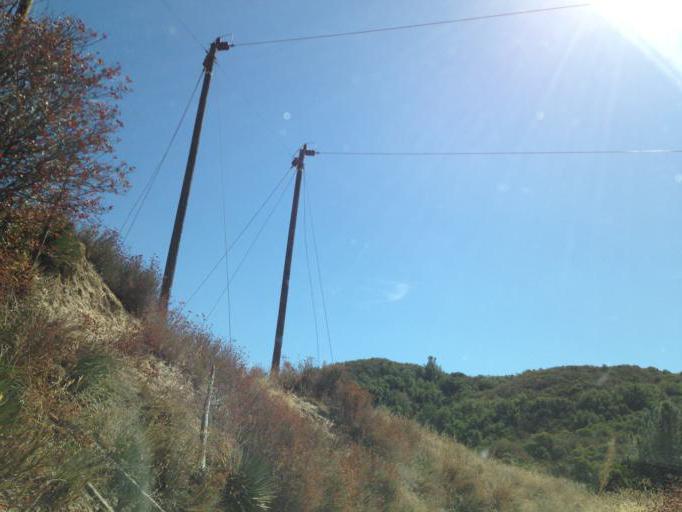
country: US
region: California
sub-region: San Bernardino County
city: Running Springs
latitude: 34.1670
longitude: -117.0685
